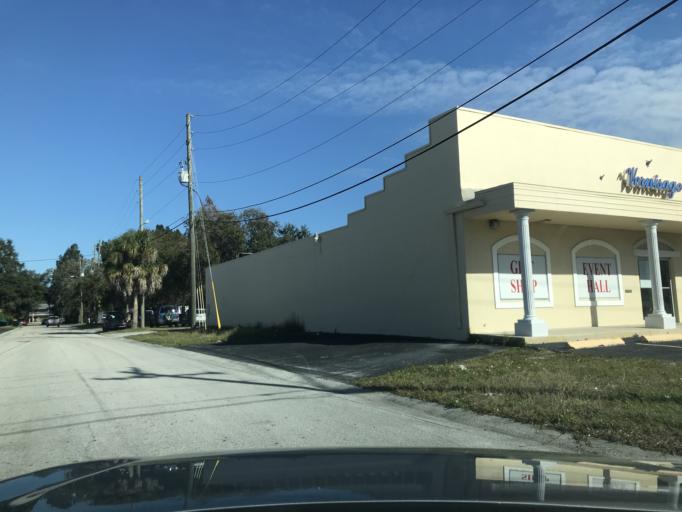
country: US
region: Florida
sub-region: Pinellas County
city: Belleair
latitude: 27.9315
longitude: -82.7894
